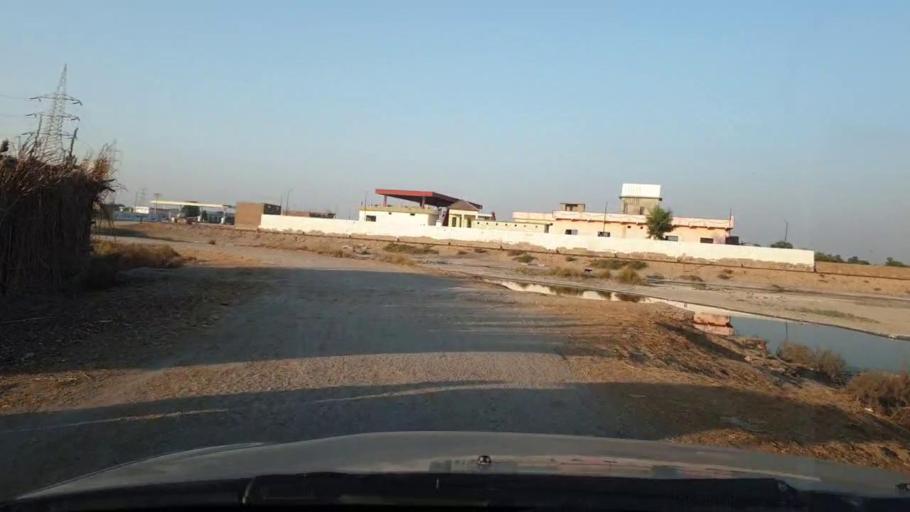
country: PK
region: Sindh
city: Matli
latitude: 25.0435
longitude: 68.6341
